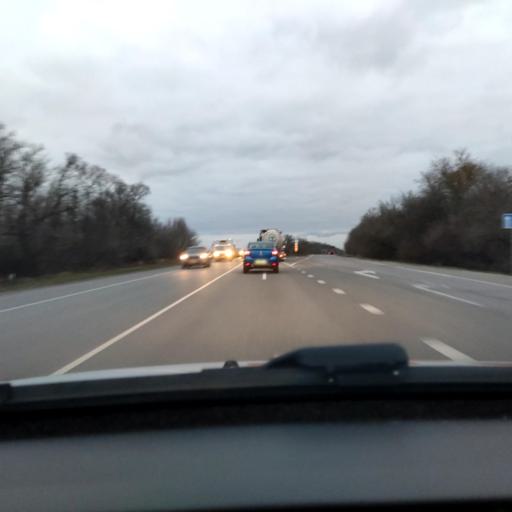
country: RU
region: Lipetsk
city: Borinskoye
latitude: 52.4578
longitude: 39.3155
